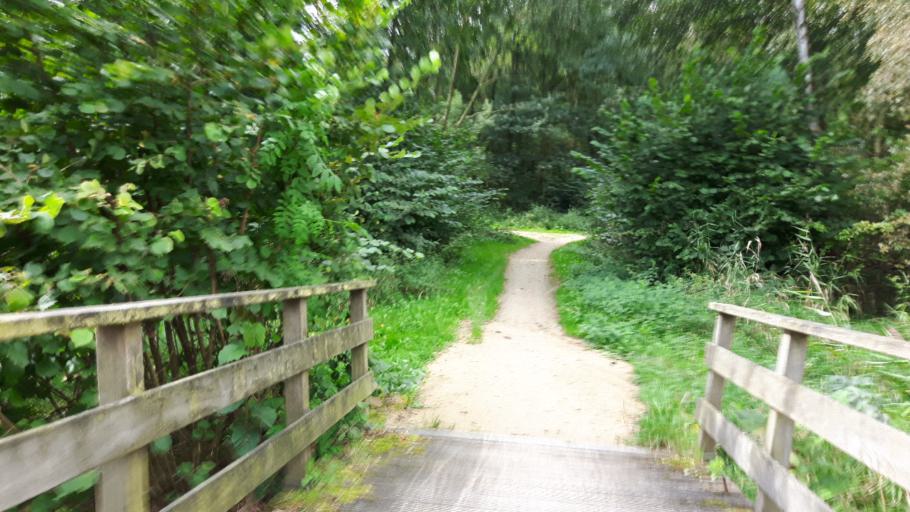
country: NL
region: Groningen
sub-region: Gemeente Slochteren
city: Slochteren
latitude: 53.2609
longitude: 6.7967
